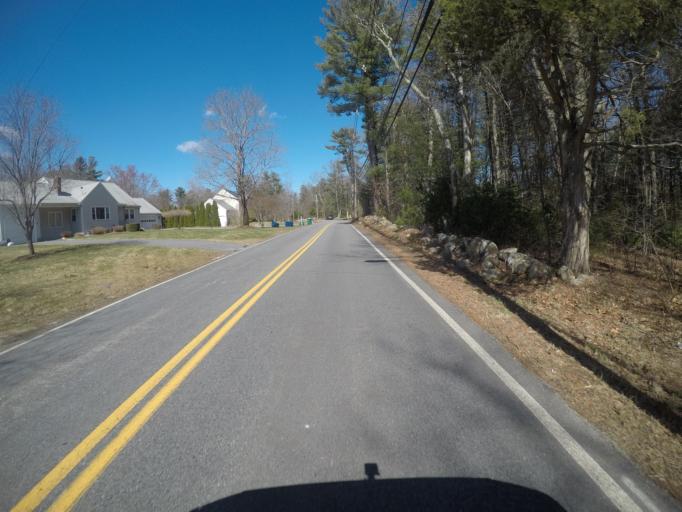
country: US
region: Massachusetts
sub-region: Bristol County
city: Easton
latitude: 42.0137
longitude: -71.0969
